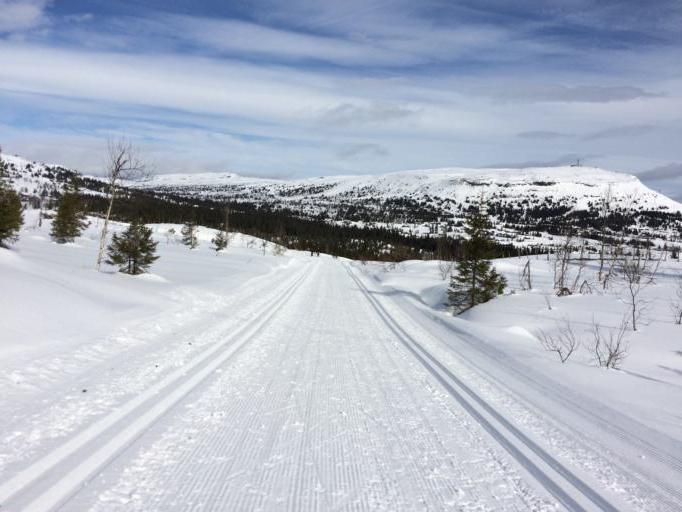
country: NO
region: Oppland
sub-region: Gausdal
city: Segalstad bru
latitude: 61.3333
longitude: 10.0502
